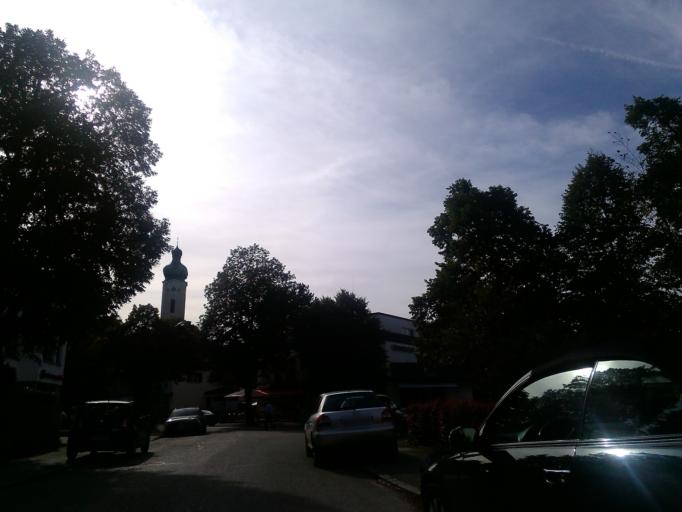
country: DE
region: Bavaria
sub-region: Upper Bavaria
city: Pullach im Isartal
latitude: 48.0776
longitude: 11.5205
